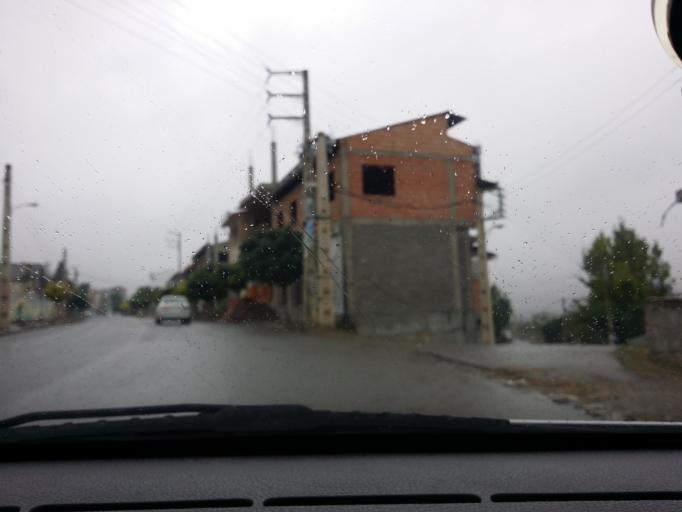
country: IR
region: Mazandaran
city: Chalus
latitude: 36.5275
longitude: 51.2307
